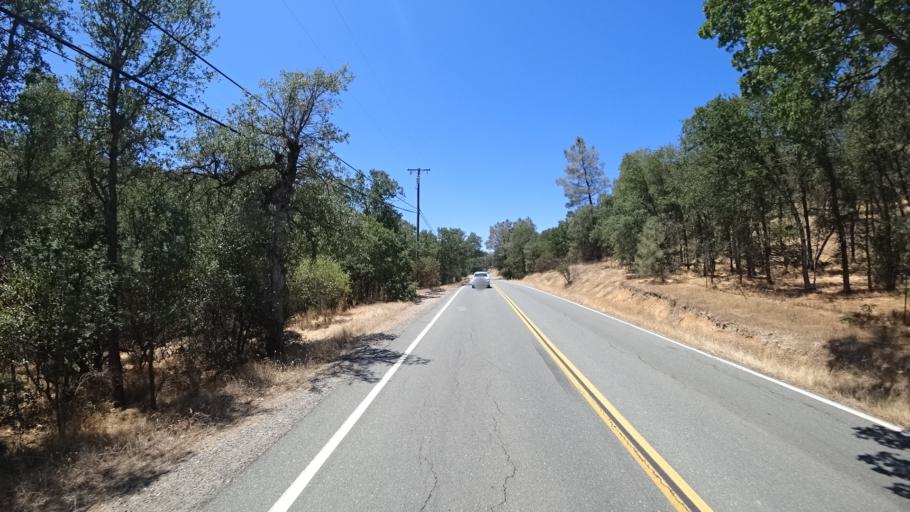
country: US
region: California
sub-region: Calaveras County
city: Valley Springs
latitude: 38.2011
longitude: -120.8873
